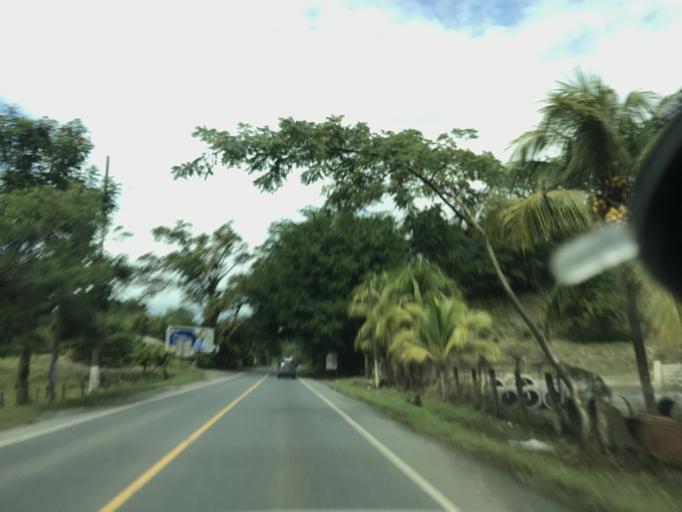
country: GT
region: Izabal
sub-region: Municipio de Puerto Barrios
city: Puerto Barrios
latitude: 15.6673
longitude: -88.5607
